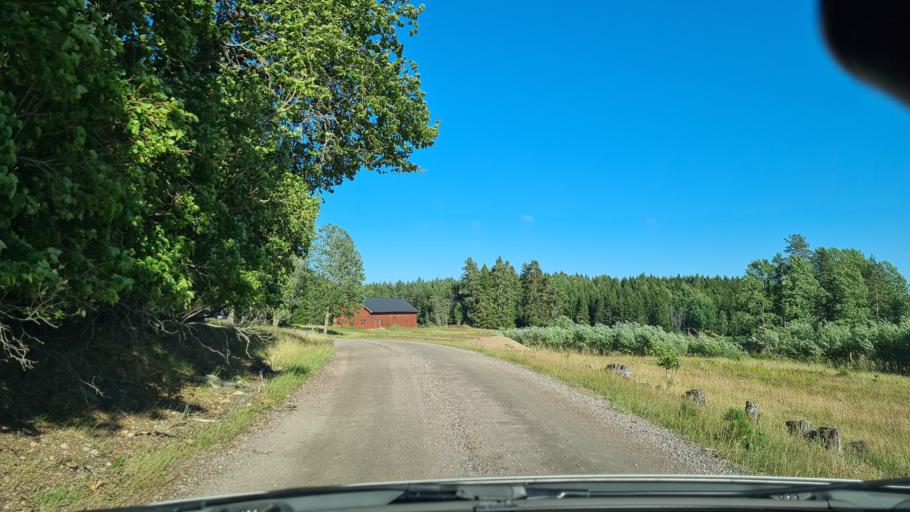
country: SE
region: Soedermanland
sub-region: Nykopings Kommun
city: Nykoping
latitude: 58.9093
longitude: 16.9251
